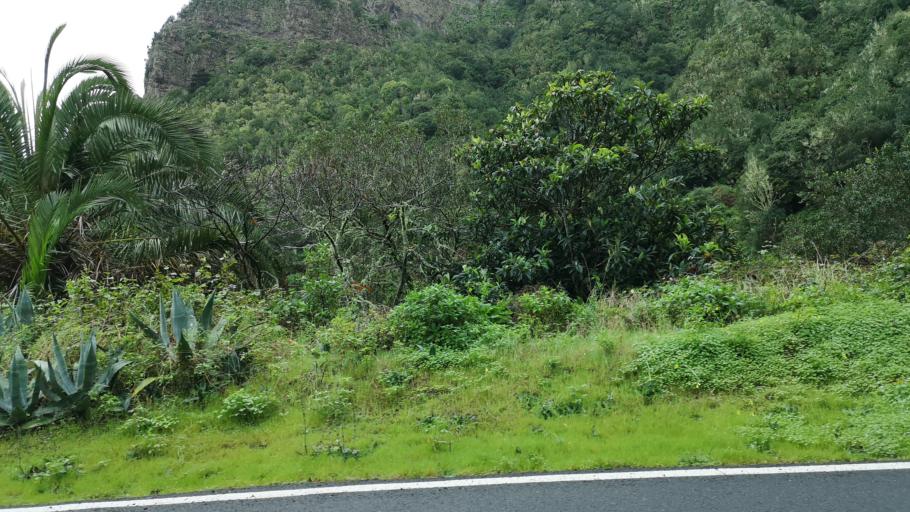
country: ES
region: Canary Islands
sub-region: Provincia de Santa Cruz de Tenerife
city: Hermigua
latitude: 28.1314
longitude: -17.2004
